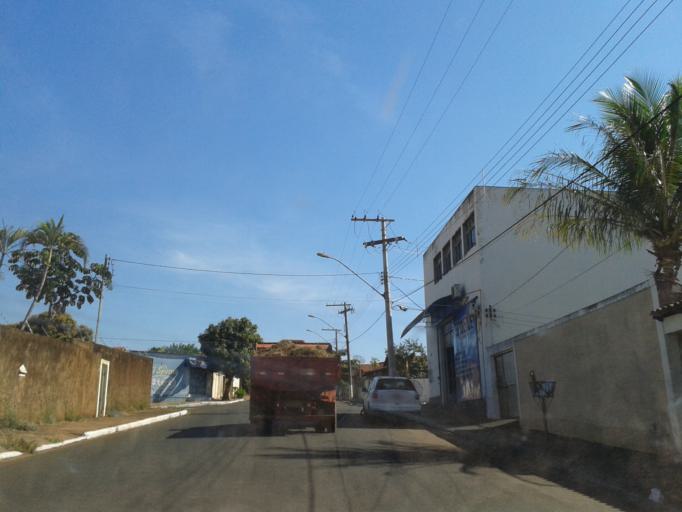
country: BR
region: Minas Gerais
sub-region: Ituiutaba
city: Ituiutaba
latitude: -18.9805
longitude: -49.4755
